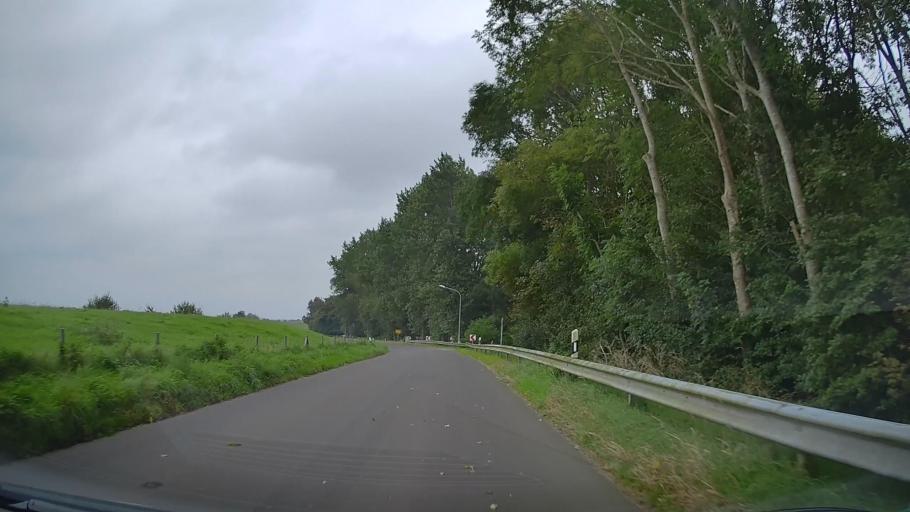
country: DE
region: Lower Saxony
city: Geversdorf
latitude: 53.8243
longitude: 9.0682
